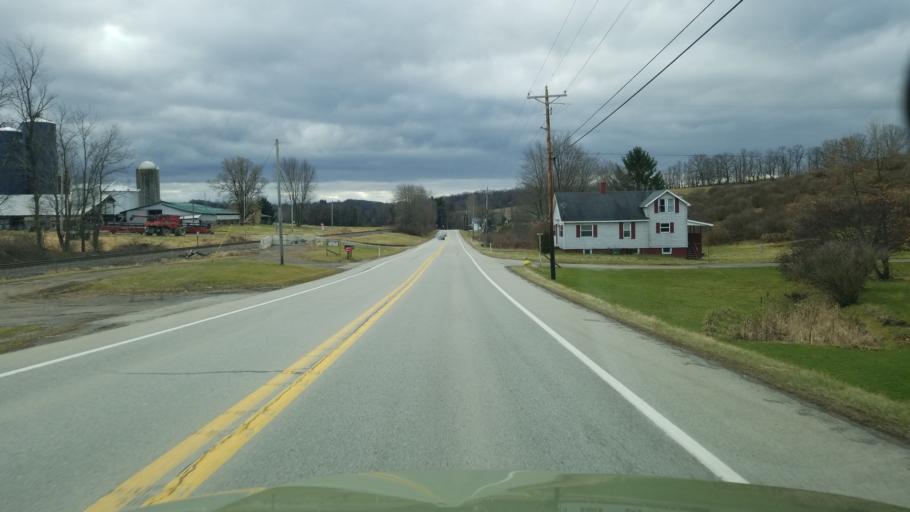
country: US
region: Pennsylvania
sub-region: Indiana County
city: Clymer
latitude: 40.7934
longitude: -79.0539
